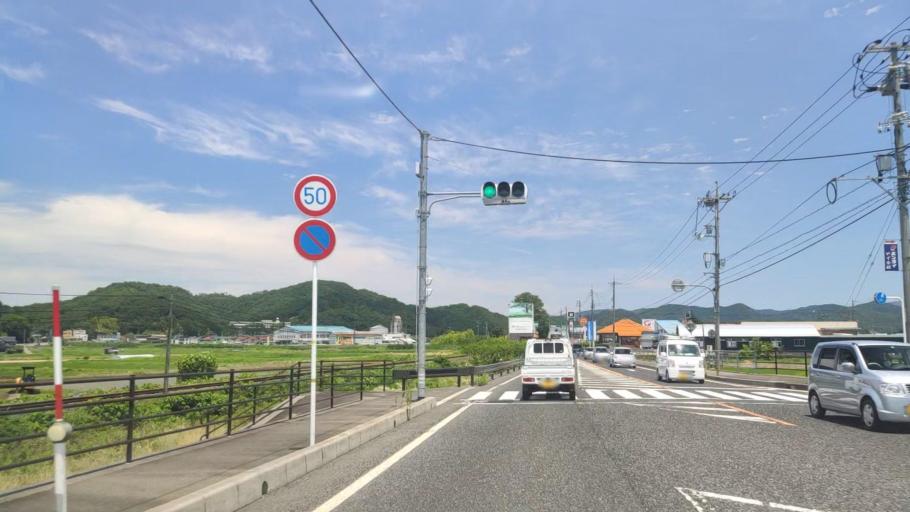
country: JP
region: Tottori
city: Tottori
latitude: 35.4202
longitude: 134.2598
